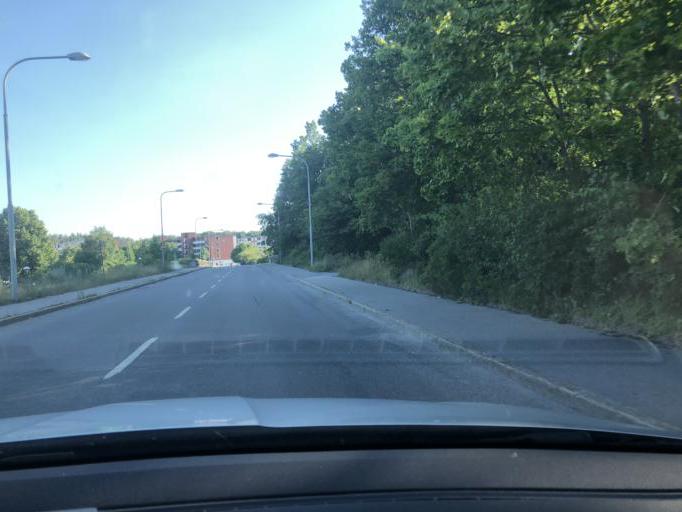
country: SE
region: Stockholm
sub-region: Botkyrka Kommun
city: Fittja
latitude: 59.2711
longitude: 17.8890
